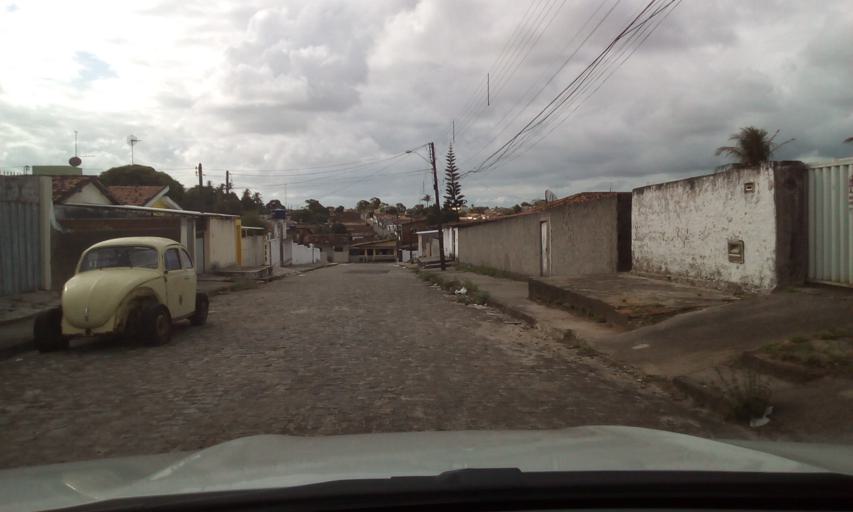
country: BR
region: Paraiba
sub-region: Joao Pessoa
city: Joao Pessoa
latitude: -7.1510
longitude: -34.8835
